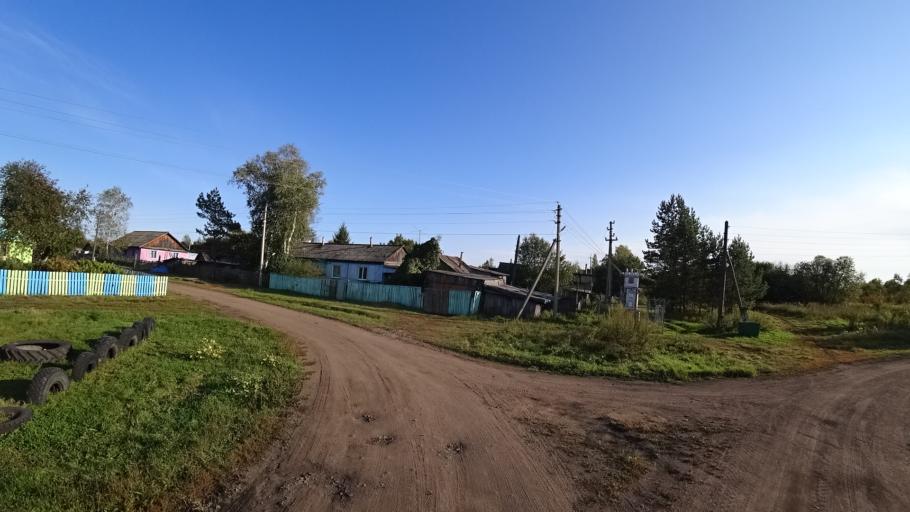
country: RU
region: Amur
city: Arkhara
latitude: 49.3554
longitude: 130.1226
